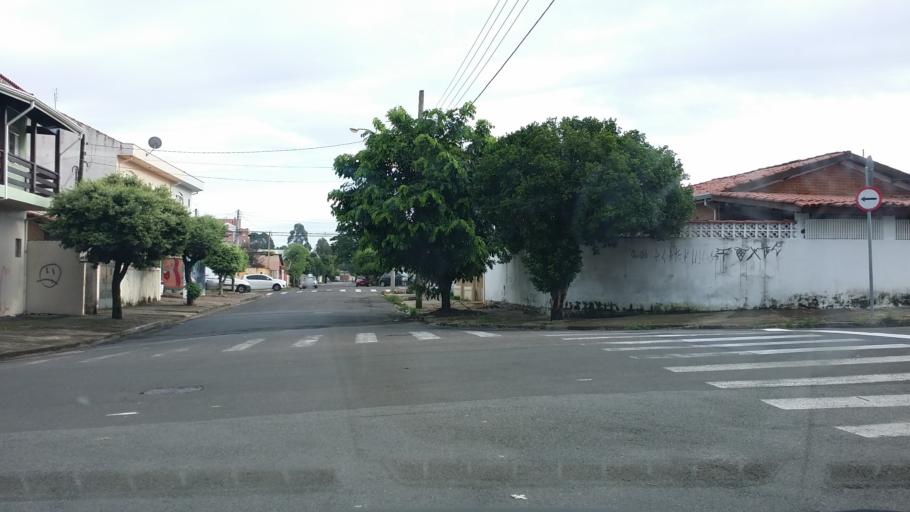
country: BR
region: Sao Paulo
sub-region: Indaiatuba
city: Indaiatuba
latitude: -23.1138
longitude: -47.2252
